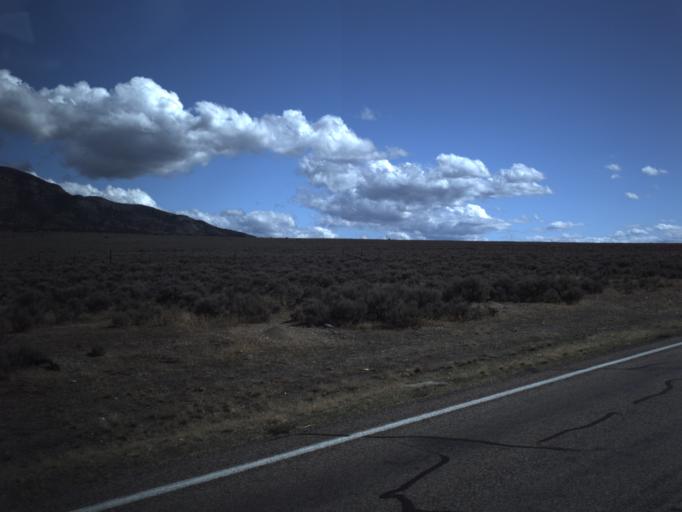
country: US
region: Utah
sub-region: Beaver County
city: Milford
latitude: 38.3162
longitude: -112.9704
